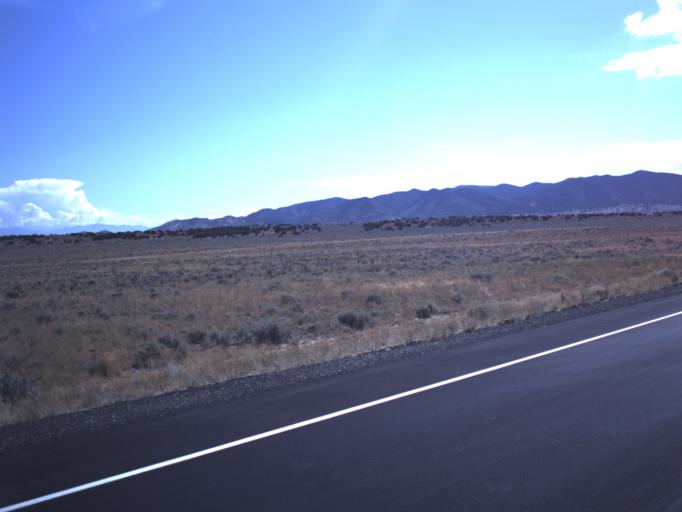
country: US
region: Utah
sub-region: Utah County
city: Eagle Mountain
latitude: 40.0585
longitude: -112.3085
